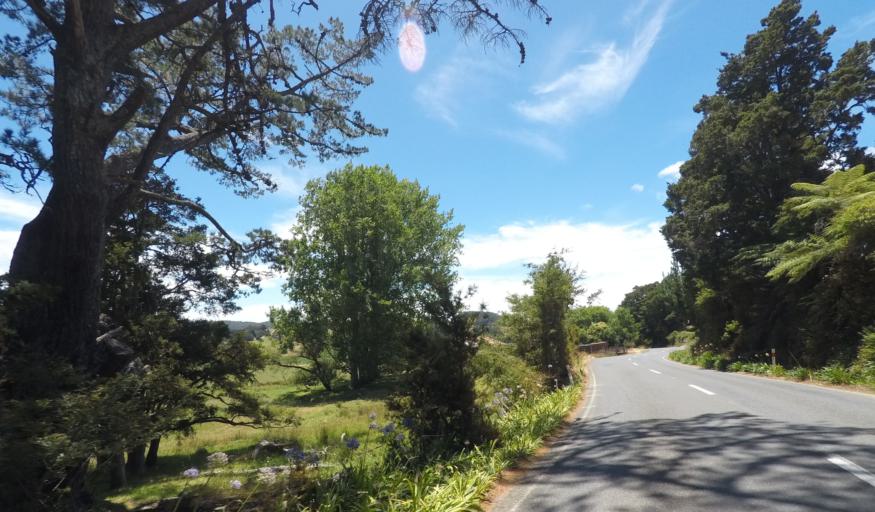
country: NZ
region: Northland
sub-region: Whangarei
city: Whangarei
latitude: -35.5363
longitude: 174.3130
